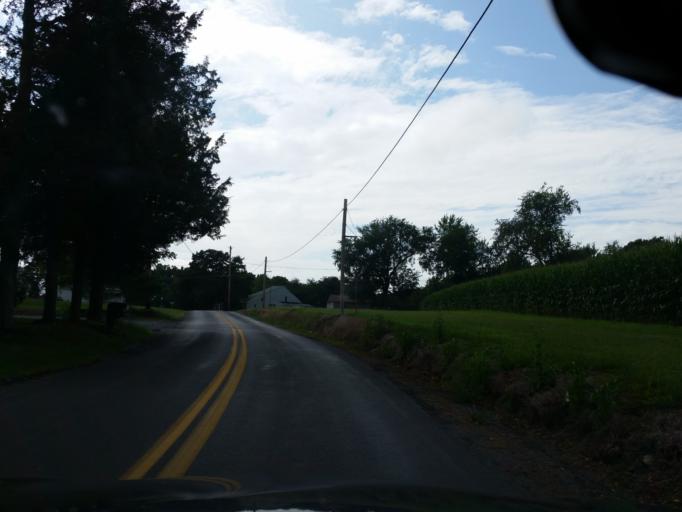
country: US
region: Pennsylvania
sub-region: Union County
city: New Columbia
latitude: 41.0339
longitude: -76.8869
